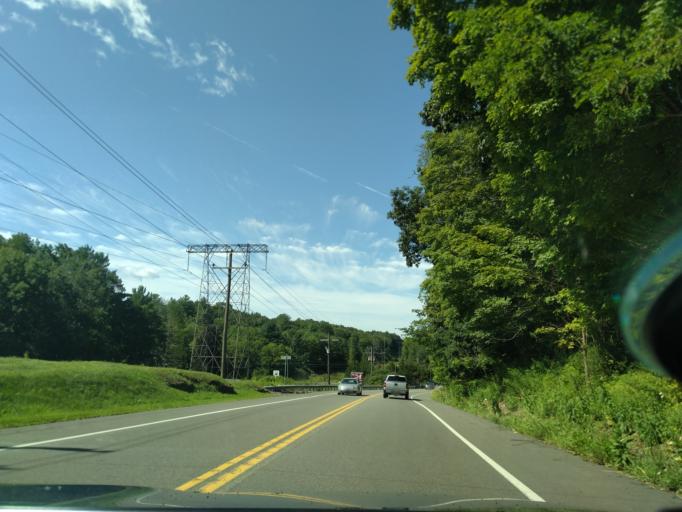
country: US
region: Pennsylvania
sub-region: Pike County
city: Saw Creek
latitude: 41.0699
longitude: -75.0418
